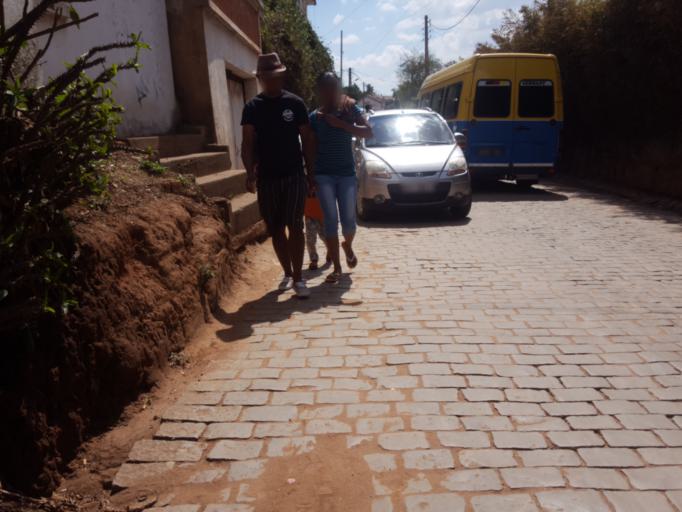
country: MG
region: Analamanga
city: Antananarivo
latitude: -18.9800
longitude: 47.5319
